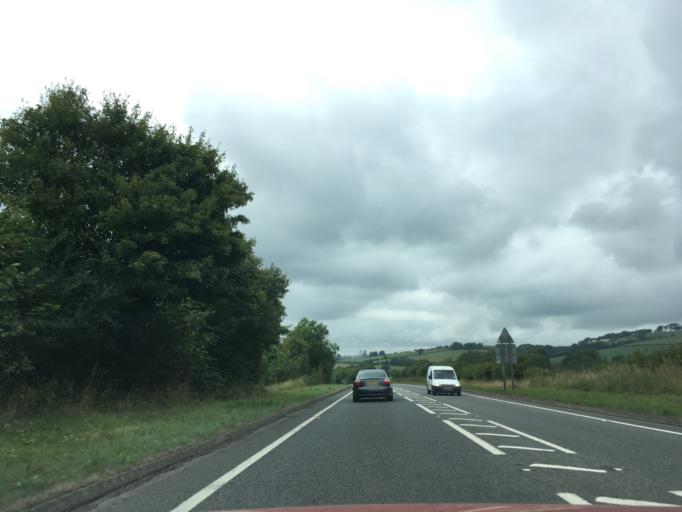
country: GB
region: Wales
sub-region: Carmarthenshire
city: Whitland
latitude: 51.8251
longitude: -4.5968
